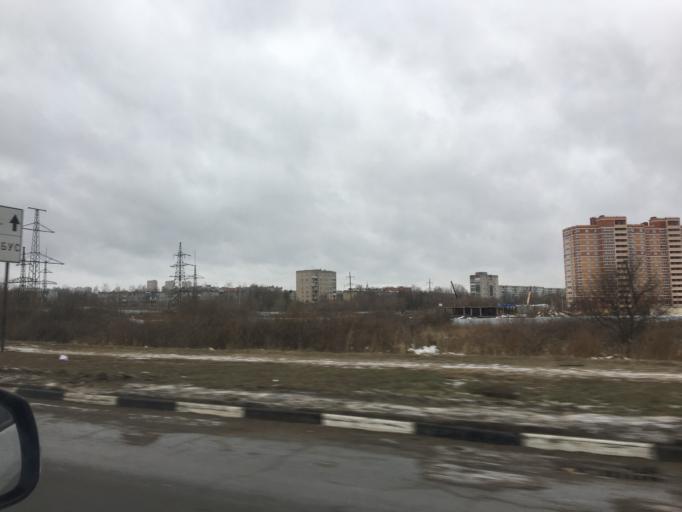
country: RU
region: Tula
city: Tula
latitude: 54.1799
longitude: 37.6474
